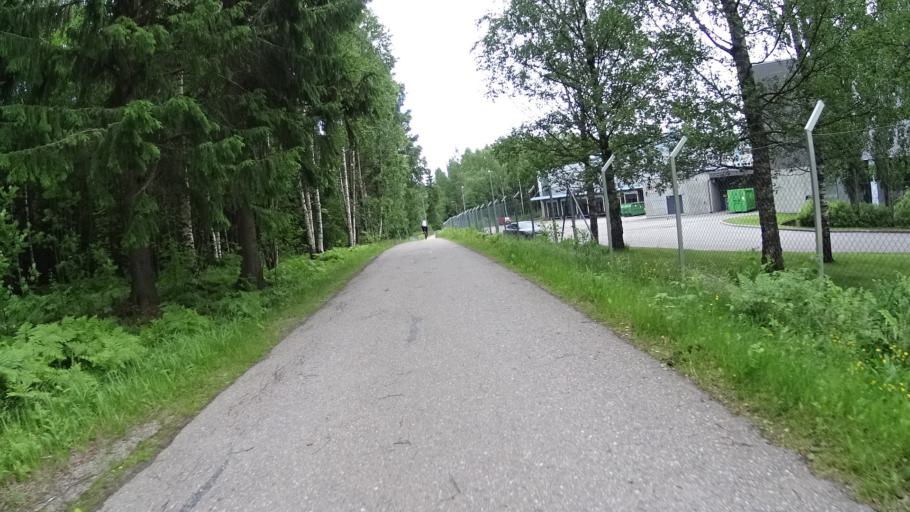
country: FI
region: Uusimaa
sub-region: Helsinki
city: Kilo
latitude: 60.2778
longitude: 24.8249
